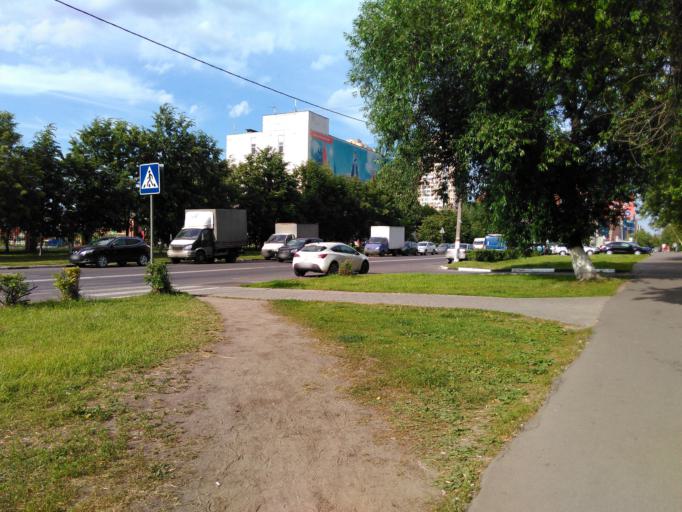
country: RU
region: Moskovskaya
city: Reutov
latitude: 55.7495
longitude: 37.8633
